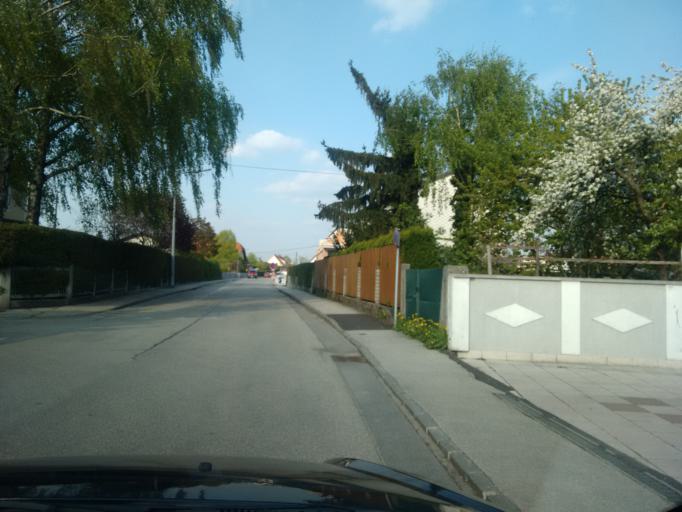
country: AT
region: Upper Austria
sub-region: Politischer Bezirk Linz-Land
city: Traun
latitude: 48.2284
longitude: 14.2508
